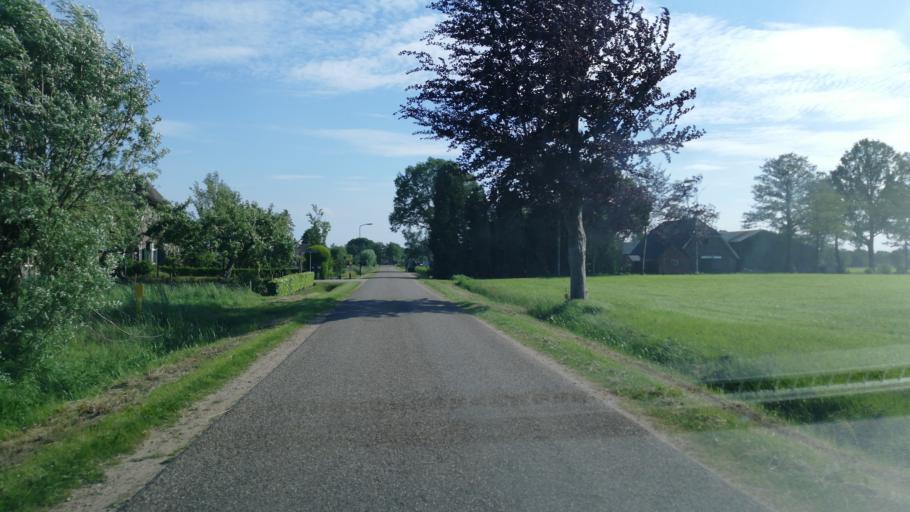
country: NL
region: Gelderland
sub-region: Gemeente Epe
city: Vaassen
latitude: 52.2619
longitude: 5.9898
